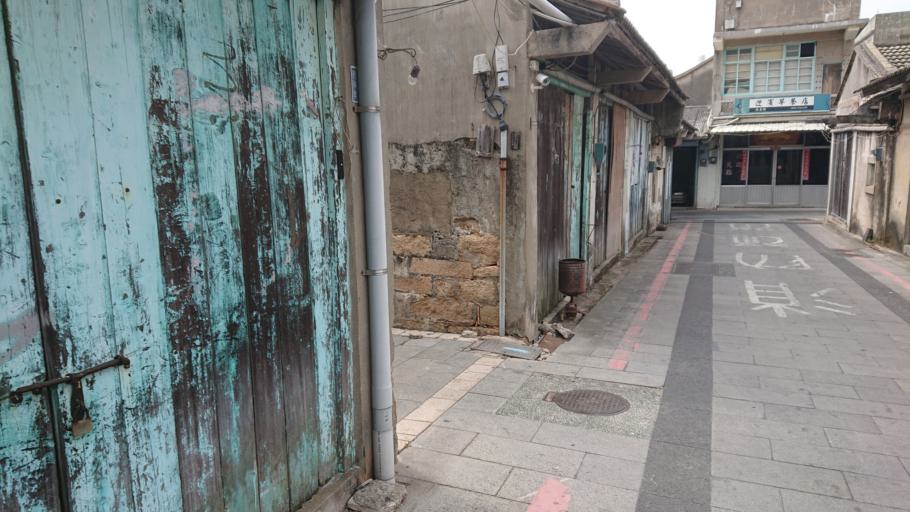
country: TW
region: Fukien
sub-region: Kinmen
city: Jincheng
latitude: 24.4287
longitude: 118.2488
